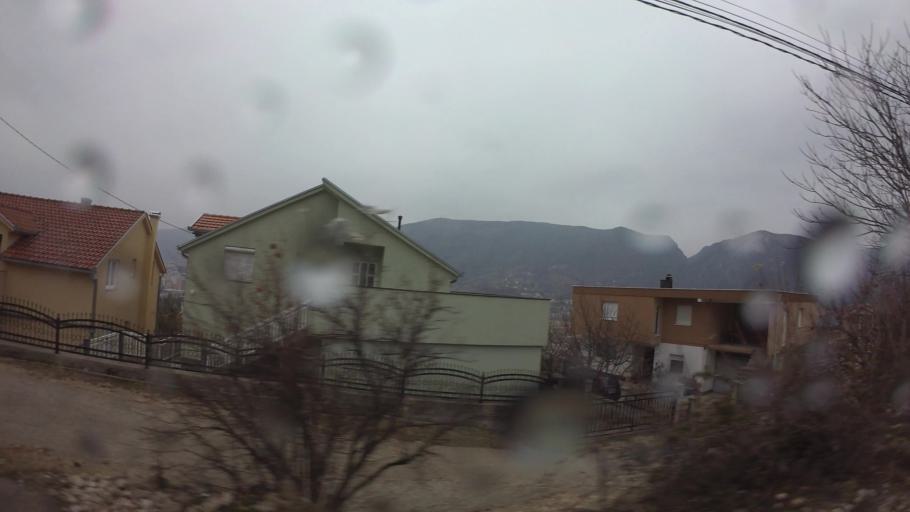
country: BA
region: Federation of Bosnia and Herzegovina
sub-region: Hercegovacko-Bosanski Kanton
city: Mostar
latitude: 43.3543
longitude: 17.8177
